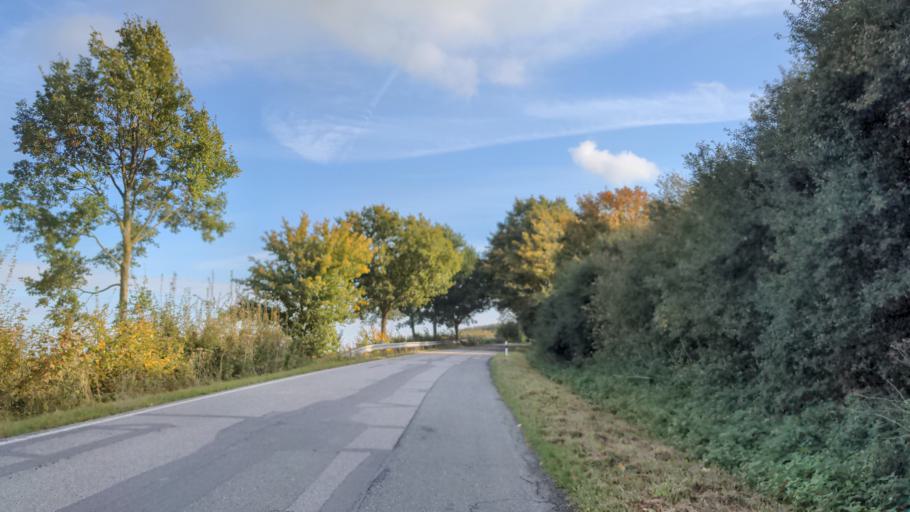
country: DE
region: Schleswig-Holstein
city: Damlos
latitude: 54.2381
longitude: 10.9138
